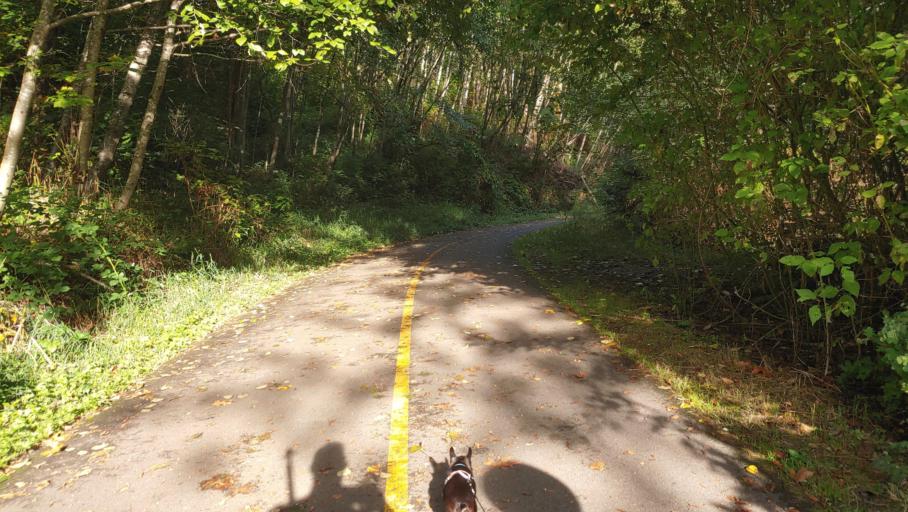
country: US
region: Washington
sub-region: King County
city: Des Moines
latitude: 47.4120
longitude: -122.3216
